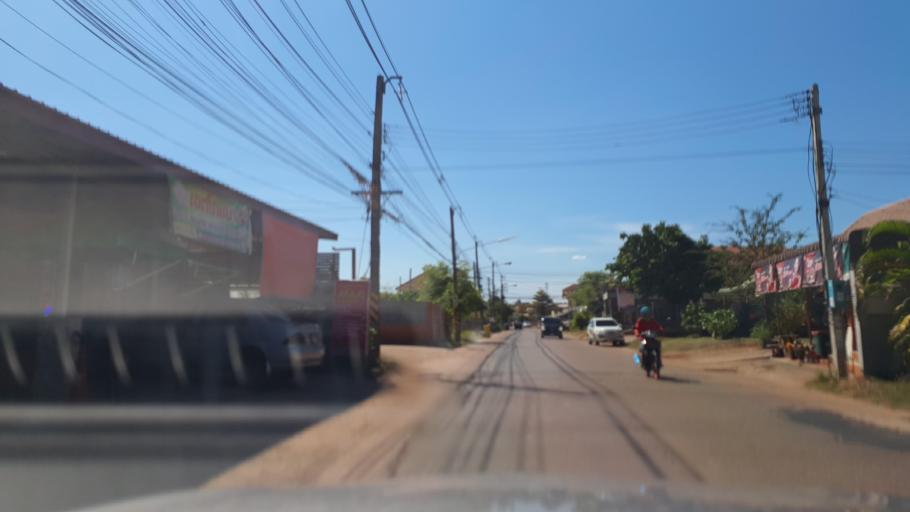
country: TH
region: Sakon Nakhon
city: Sakon Nakhon
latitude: 17.1612
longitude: 104.1224
